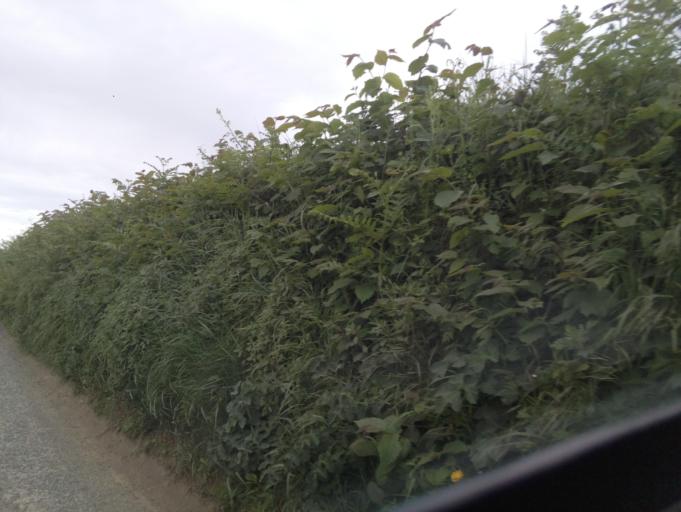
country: GB
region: England
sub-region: Devon
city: Dartmouth
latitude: 50.3236
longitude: -3.6386
